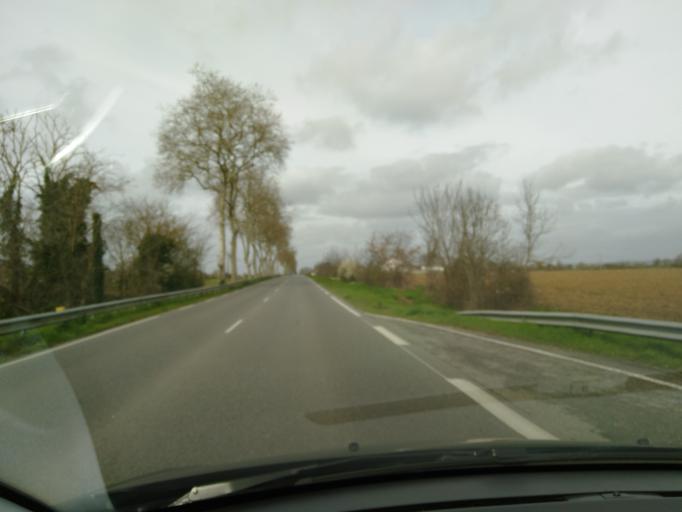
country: FR
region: Midi-Pyrenees
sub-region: Departement de la Haute-Garonne
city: Merville
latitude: 43.7239
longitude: 1.3268
